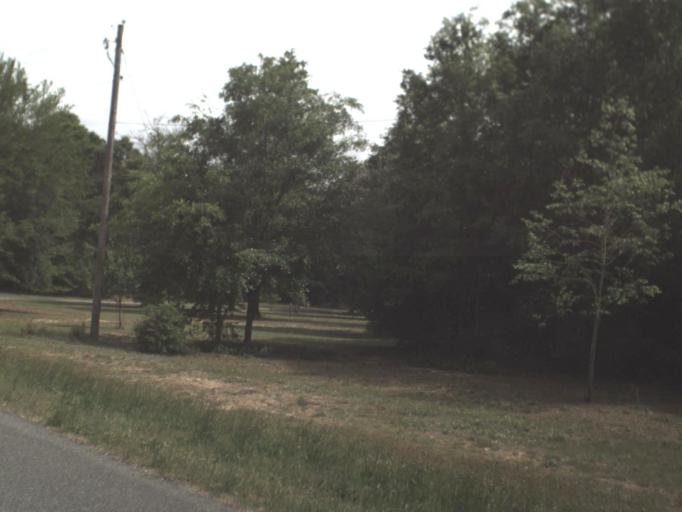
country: US
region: Florida
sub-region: Santa Rosa County
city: Point Baker
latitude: 30.7324
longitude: -87.0907
